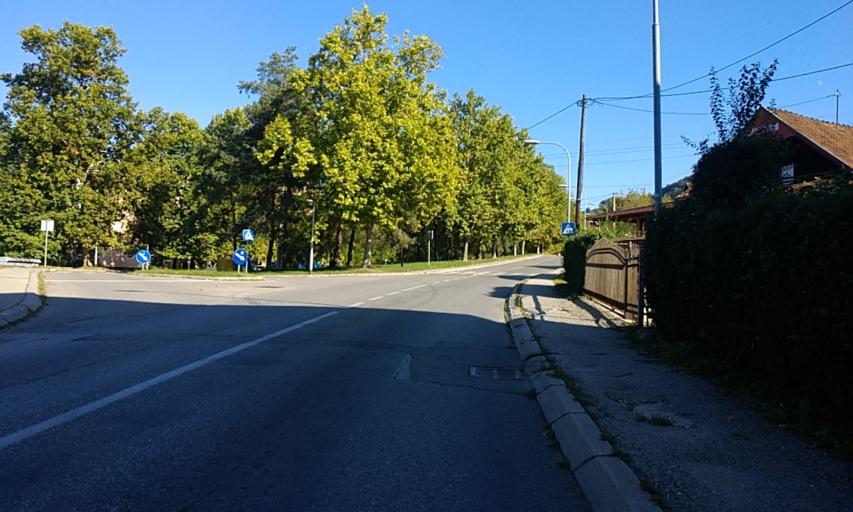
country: BA
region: Republika Srpska
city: Starcevica
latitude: 44.7593
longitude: 17.2035
